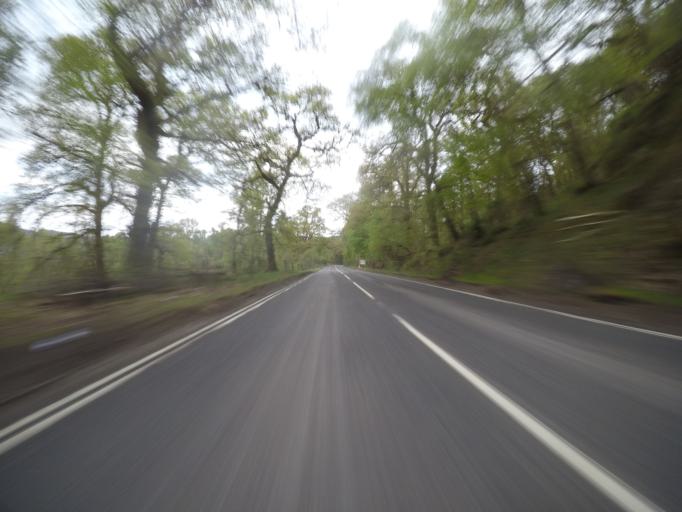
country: GB
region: Scotland
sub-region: Highland
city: Spean Bridge
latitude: 57.1518
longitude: -4.6781
